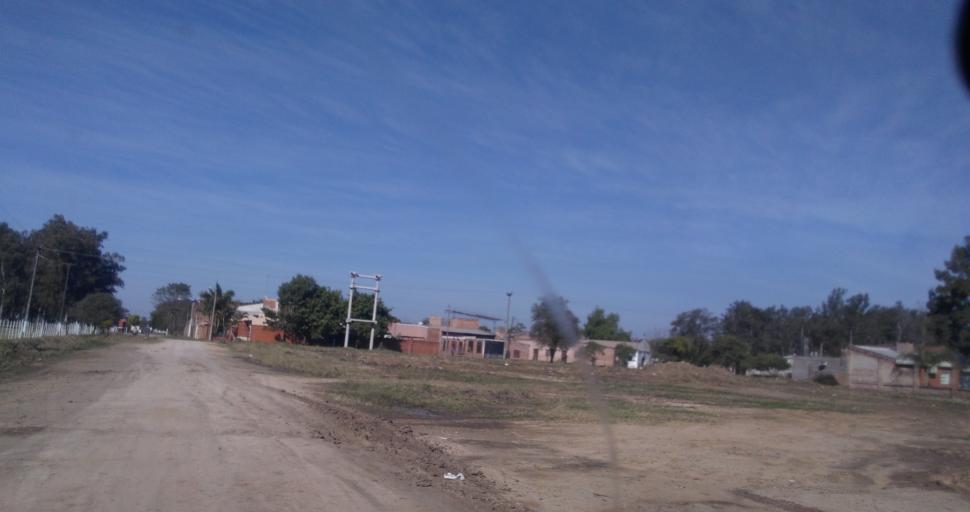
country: AR
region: Chaco
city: Fontana
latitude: -27.4429
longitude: -59.0283
